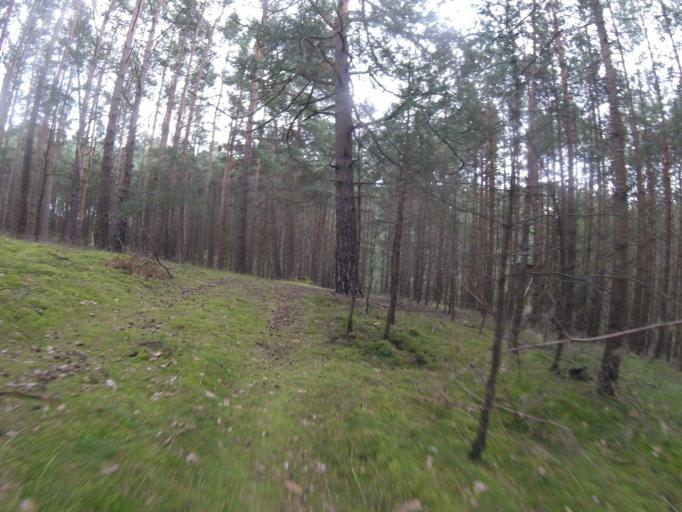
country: DE
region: Brandenburg
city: Bestensee
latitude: 52.2132
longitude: 13.6441
